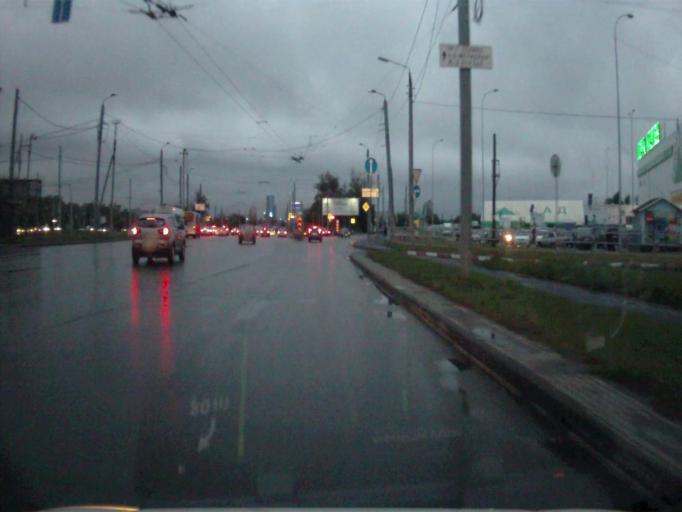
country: RU
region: Chelyabinsk
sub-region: Gorod Chelyabinsk
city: Chelyabinsk
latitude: 55.1449
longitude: 61.4496
